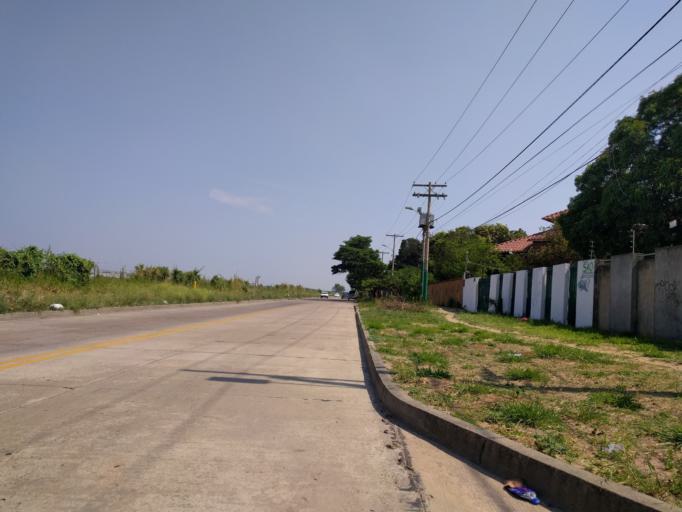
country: BO
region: Santa Cruz
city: Santa Cruz de la Sierra
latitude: -17.8121
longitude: -63.1694
